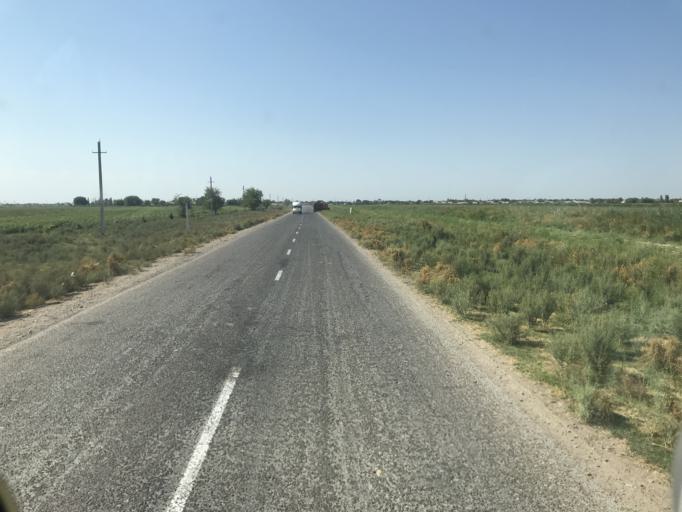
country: KZ
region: Ongtustik Qazaqstan
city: Myrzakent
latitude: 40.6816
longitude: 68.5564
